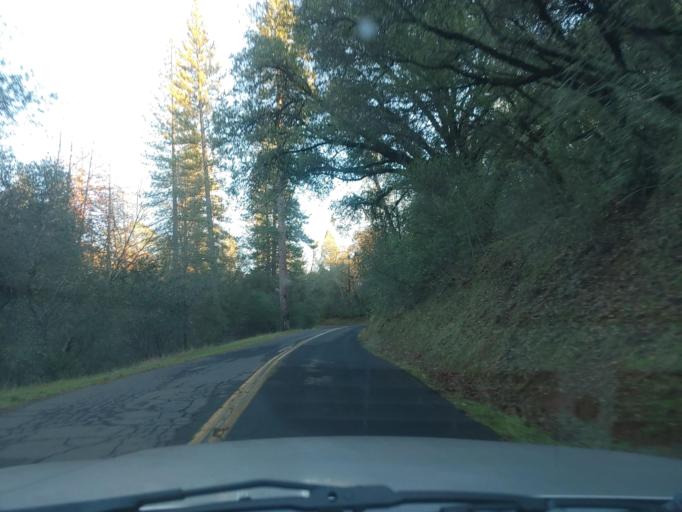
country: US
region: California
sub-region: Tuolumne County
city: Columbia
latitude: 38.0381
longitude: -120.3747
